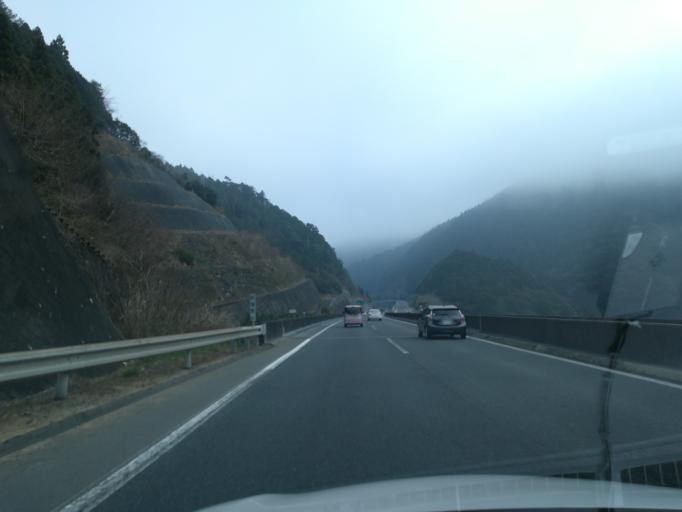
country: JP
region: Ehime
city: Kawanoecho
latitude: 33.7851
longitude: 133.6627
